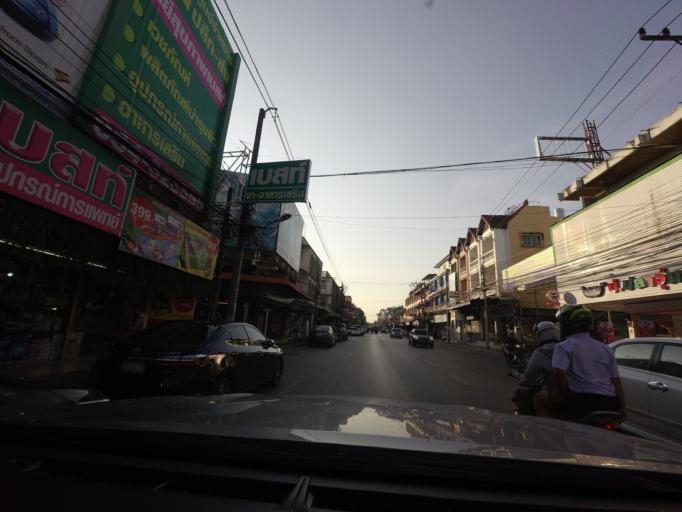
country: TH
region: Lampang
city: Lampang
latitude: 18.2892
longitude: 99.4882
